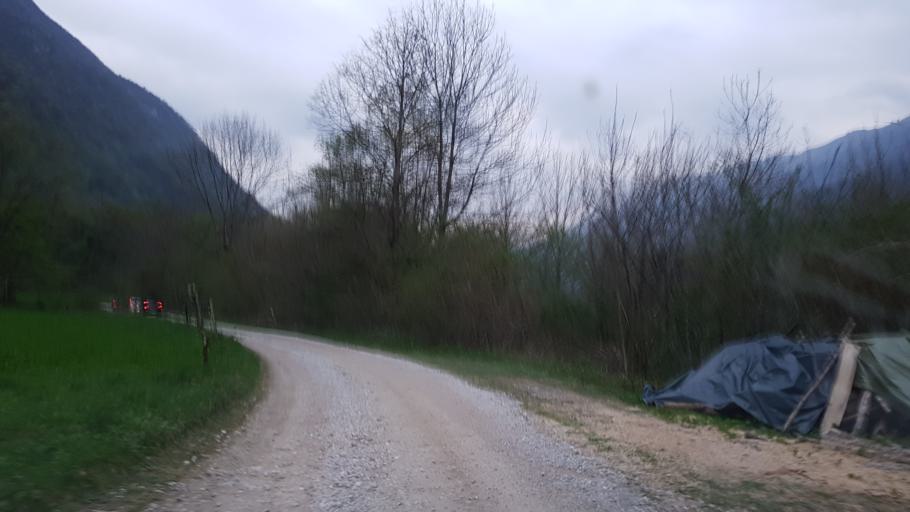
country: SI
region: Kobarid
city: Kobarid
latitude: 46.2407
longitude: 13.5417
